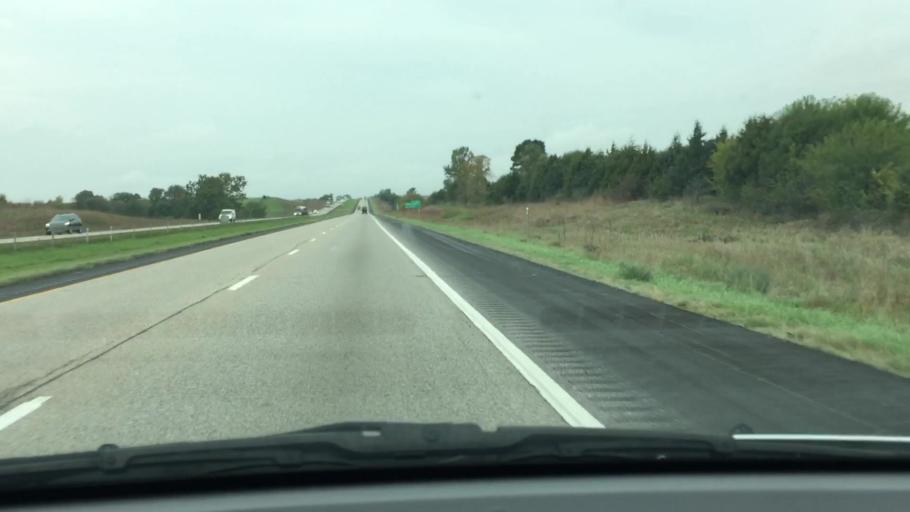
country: US
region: Iowa
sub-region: Muscatine County
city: West Liberty
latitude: 41.6610
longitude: -91.2219
